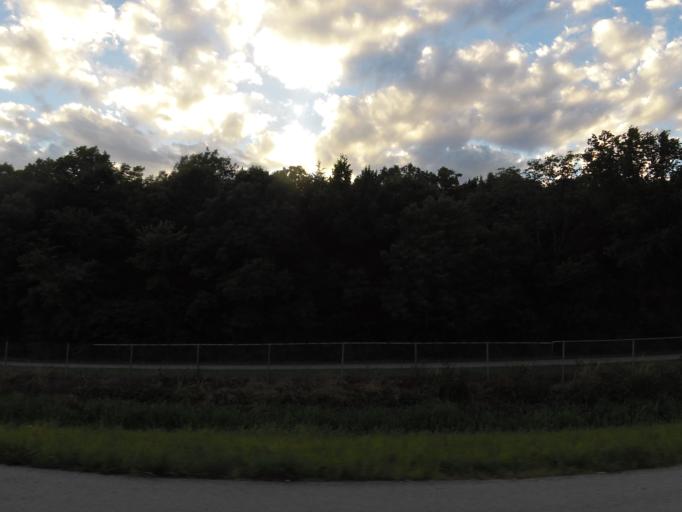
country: US
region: Missouri
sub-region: Jefferson County
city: Cedar Hill
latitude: 38.3427
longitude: -90.6528
